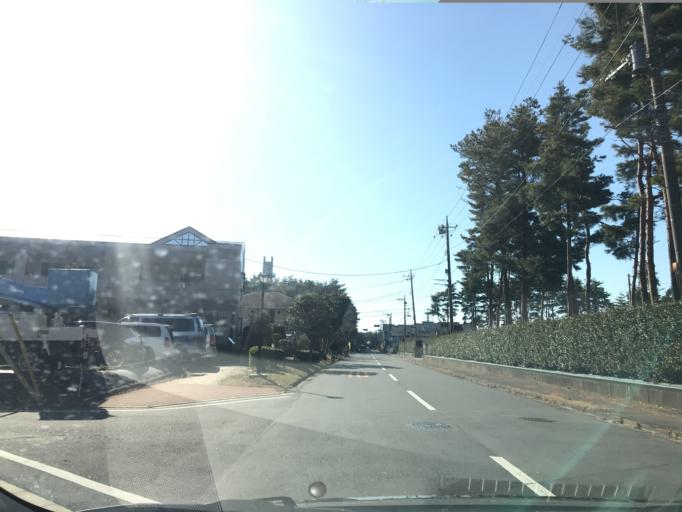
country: JP
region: Ibaraki
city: Tsukuba
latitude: 36.1295
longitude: 140.0875
